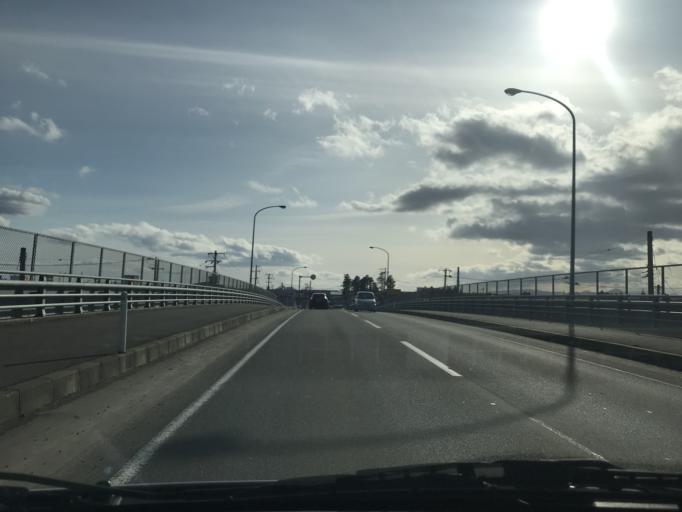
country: JP
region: Iwate
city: Kitakami
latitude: 39.2961
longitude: 141.0979
